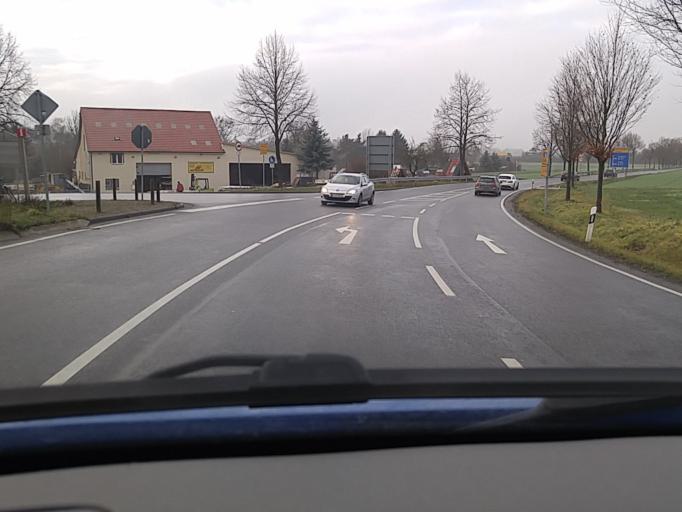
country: DE
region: Hesse
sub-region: Regierungsbezirk Darmstadt
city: Ober-Morlen
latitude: 50.3822
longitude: 8.7132
